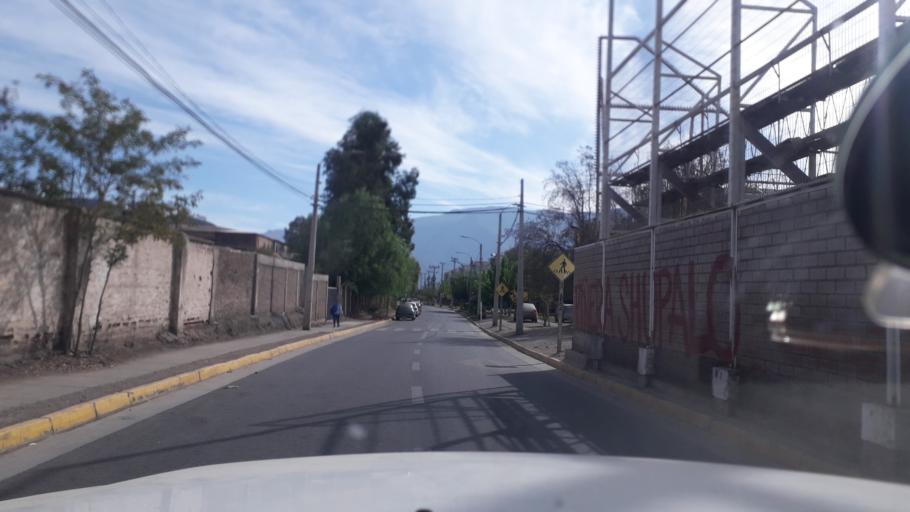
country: CL
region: Valparaiso
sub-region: Provincia de San Felipe
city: San Felipe
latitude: -32.7475
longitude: -70.7306
